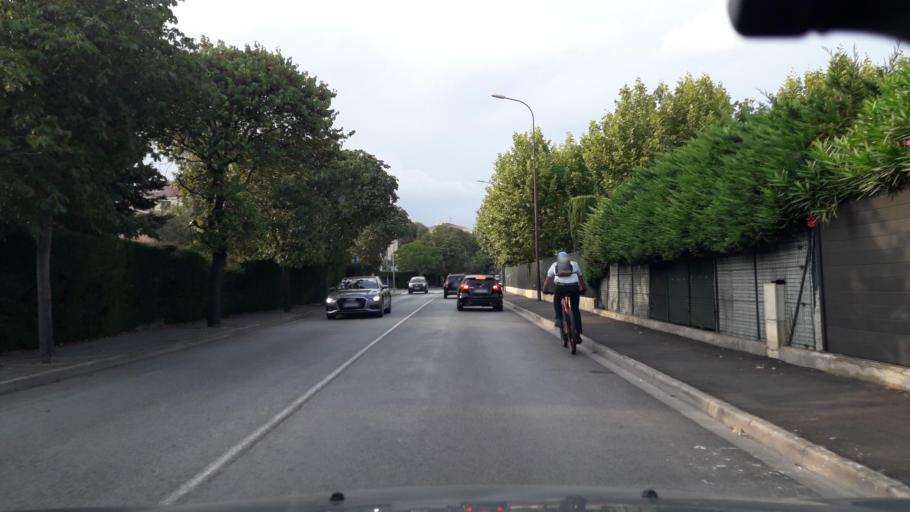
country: FR
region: Provence-Alpes-Cote d'Azur
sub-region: Departement du Var
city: Frejus
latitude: 43.4351
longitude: 6.7540
